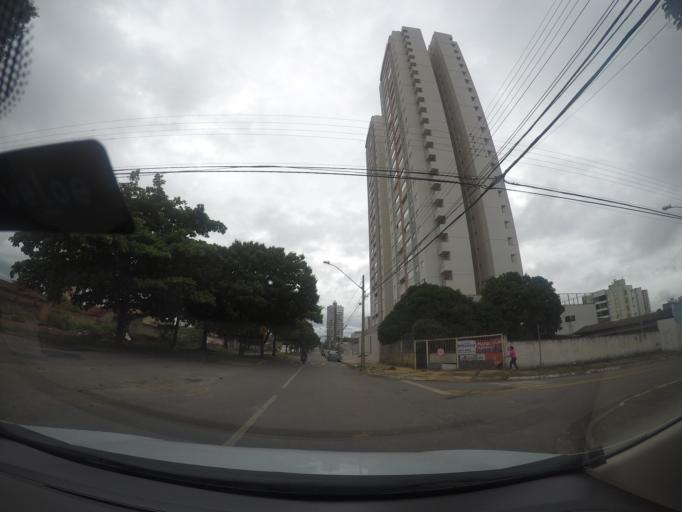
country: BR
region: Goias
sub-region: Goiania
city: Goiania
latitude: -16.7319
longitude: -49.2764
